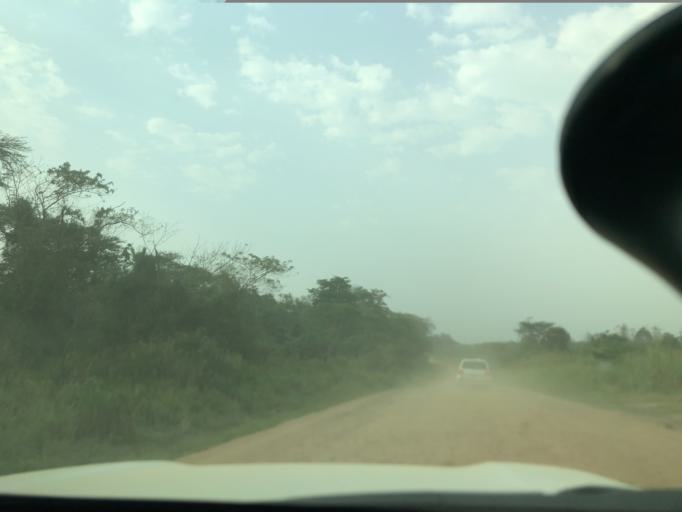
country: UG
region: Western Region
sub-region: Kasese District
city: Margherita
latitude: 0.2246
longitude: 29.6790
